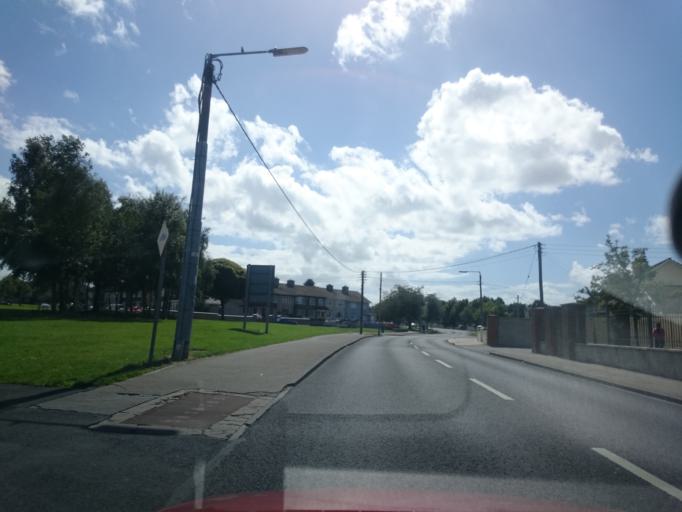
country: IE
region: Leinster
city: Clondalkin
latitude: 53.3158
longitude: -6.3964
